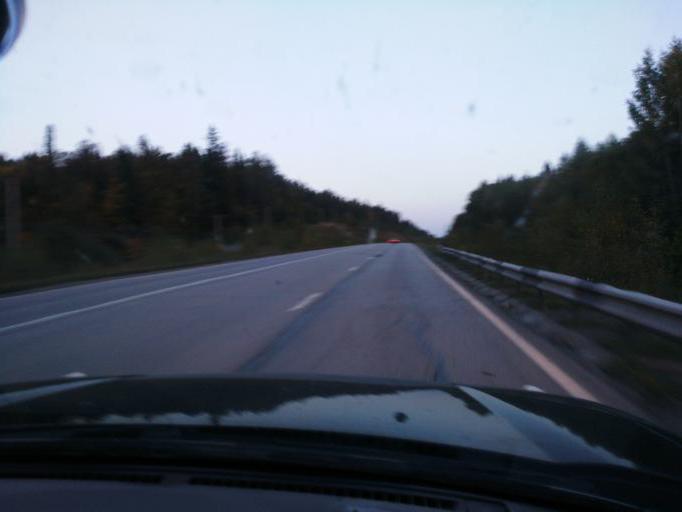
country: RU
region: Perm
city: Verkhnechusovskiye Gorodki
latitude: 58.2788
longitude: 56.9276
